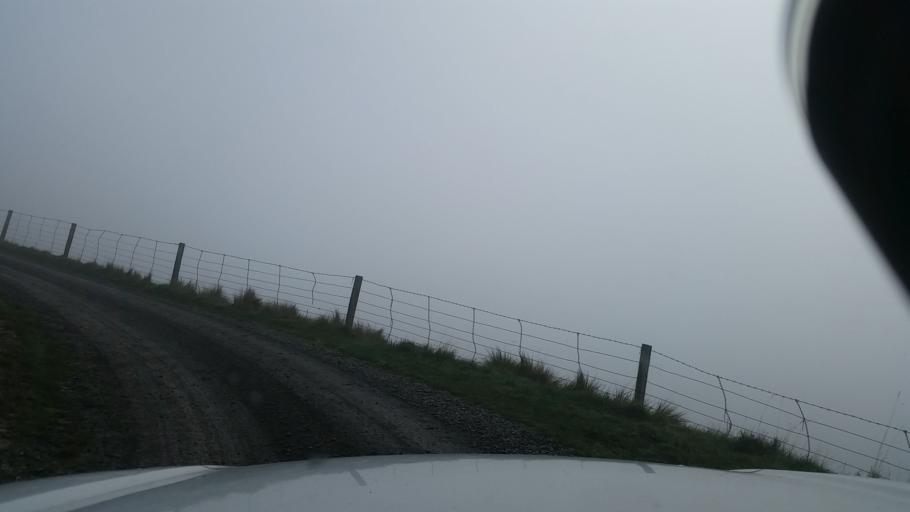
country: NZ
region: Canterbury
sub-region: Christchurch City
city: Christchurch
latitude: -43.6478
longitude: 172.8894
